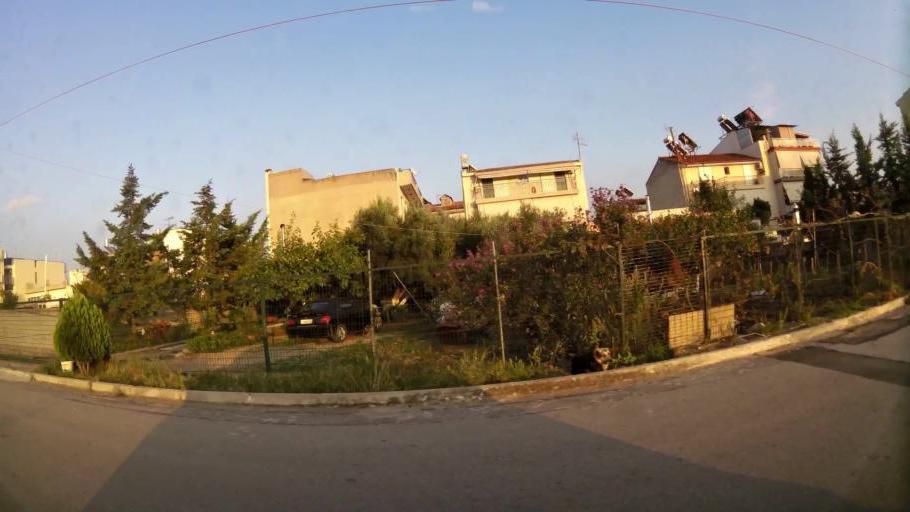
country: GR
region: Attica
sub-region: Nomarchia Anatolikis Attikis
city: Acharnes
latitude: 38.0912
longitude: 23.7413
